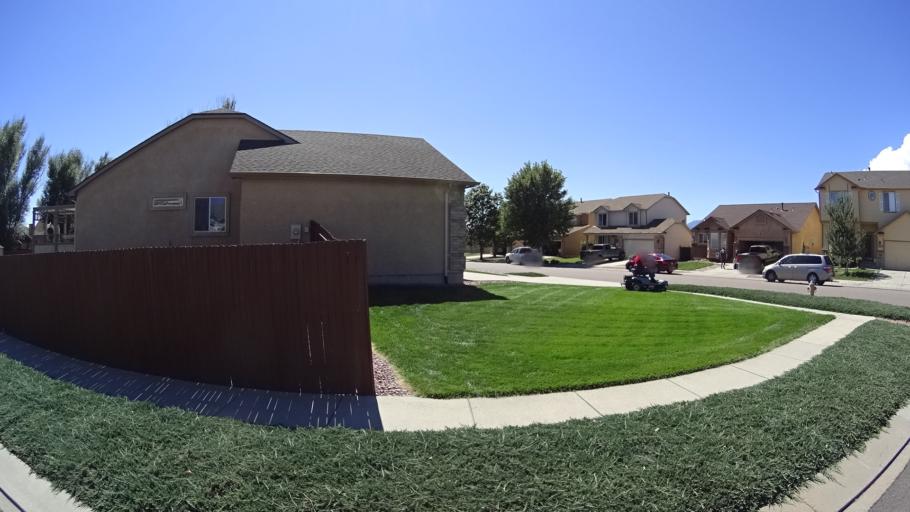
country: US
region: Colorado
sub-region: El Paso County
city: Security-Widefield
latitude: 38.7838
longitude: -104.7316
